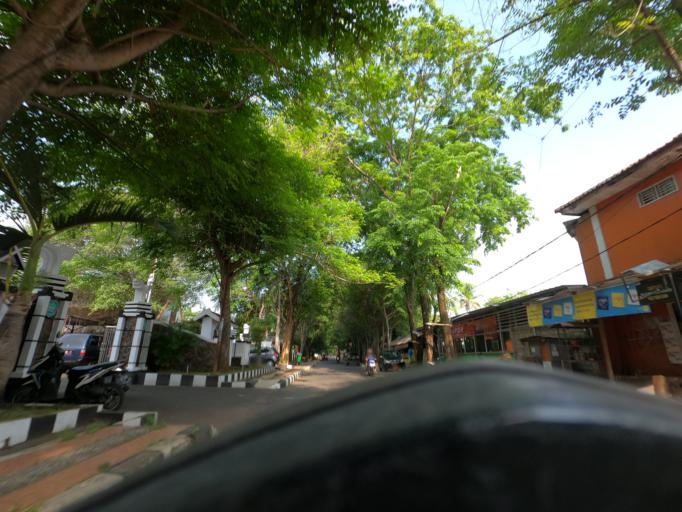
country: ID
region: West Java
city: Lembang
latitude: -6.5746
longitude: 107.7650
